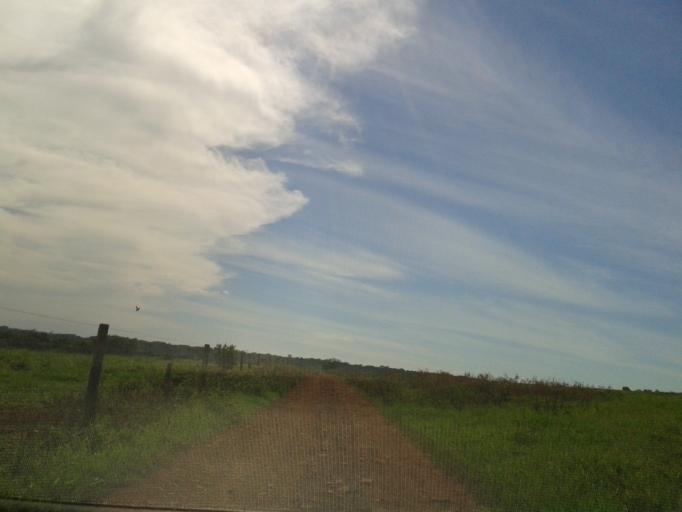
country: BR
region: Minas Gerais
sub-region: Capinopolis
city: Capinopolis
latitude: -18.6243
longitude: -49.7428
